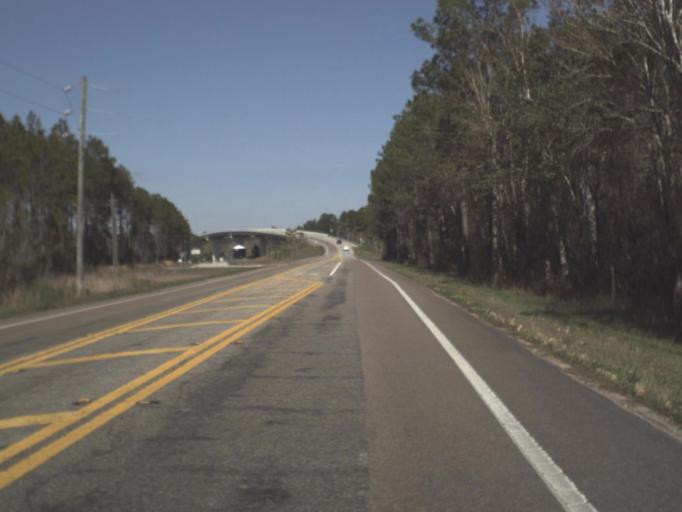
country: US
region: Florida
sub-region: Gulf County
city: Port Saint Joe
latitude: 29.8751
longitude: -85.2272
